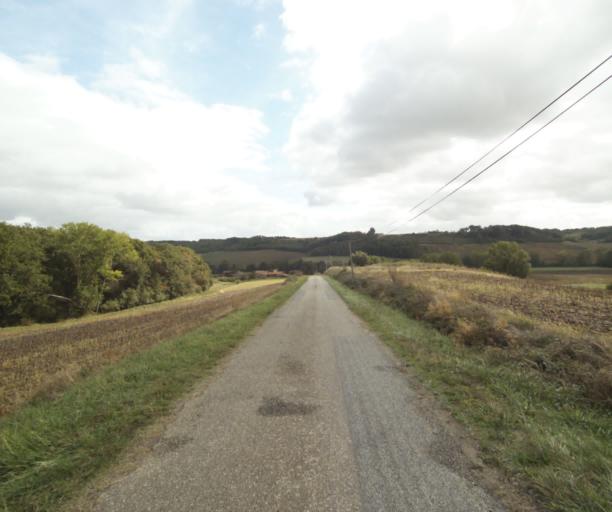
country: FR
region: Midi-Pyrenees
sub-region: Departement du Tarn-et-Garonne
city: Beaumont-de-Lomagne
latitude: 43.8684
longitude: 1.1054
